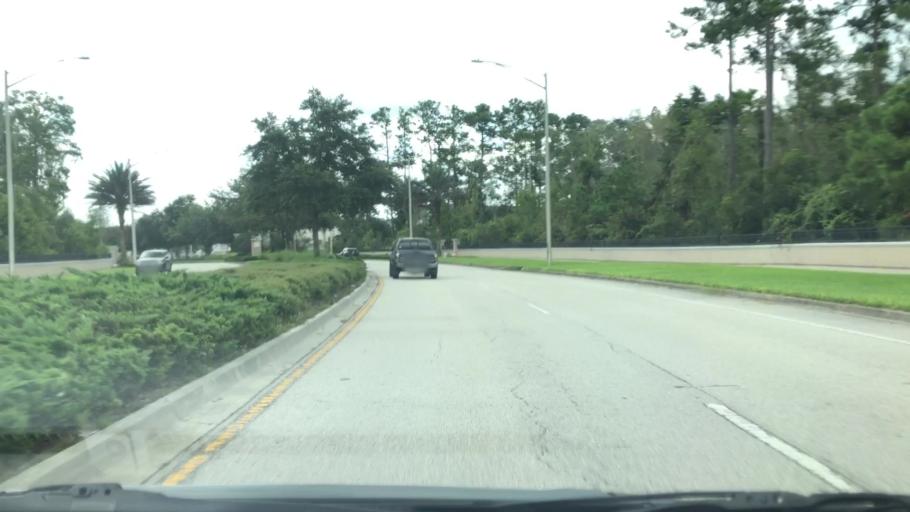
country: US
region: Florida
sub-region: Saint Johns County
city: Fruit Cove
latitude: 30.1236
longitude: -81.5306
